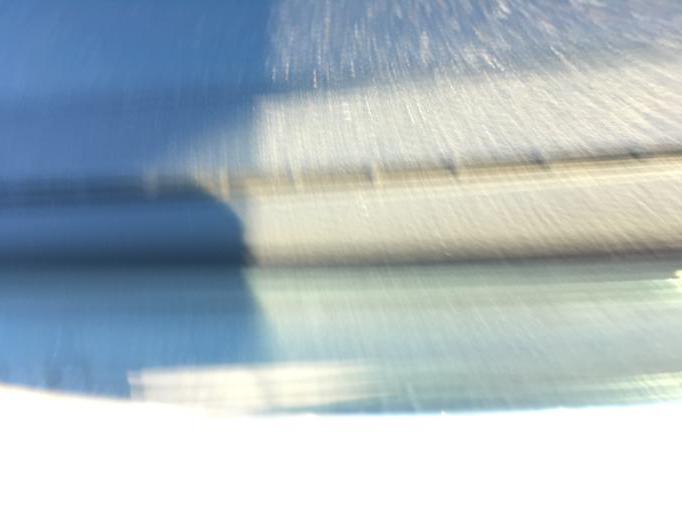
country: US
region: Colorado
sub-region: Delta County
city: Delta
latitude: 38.7555
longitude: -108.1746
